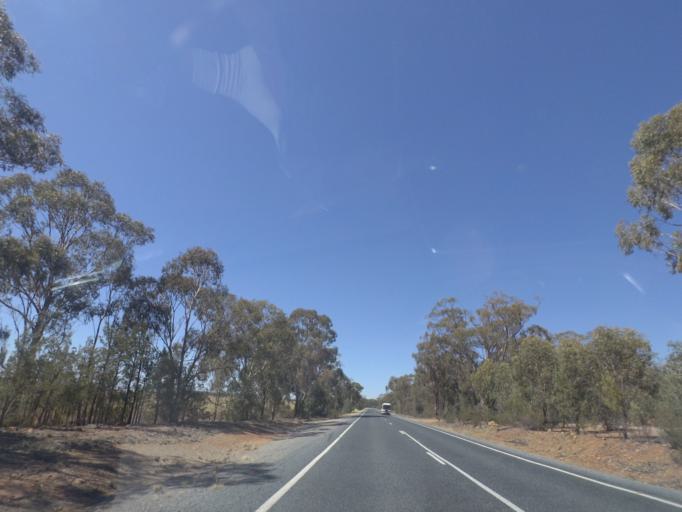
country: AU
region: New South Wales
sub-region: Narrandera
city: Narrandera
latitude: -34.4358
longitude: 146.8423
